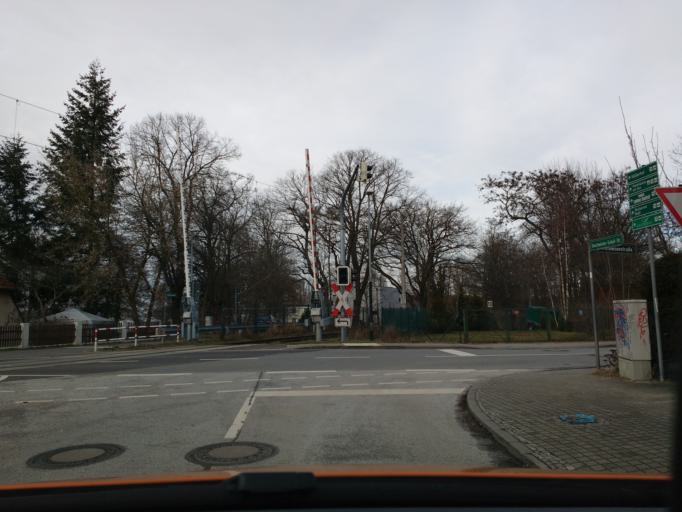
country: DE
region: Brandenburg
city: Michendorf
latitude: 52.3413
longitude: 12.9807
